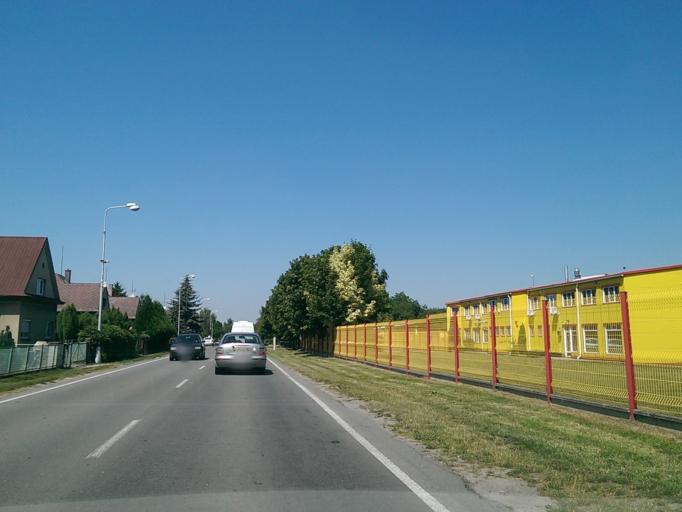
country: CZ
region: Central Bohemia
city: Benatky nad Jizerou
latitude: 50.3056
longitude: 14.8539
